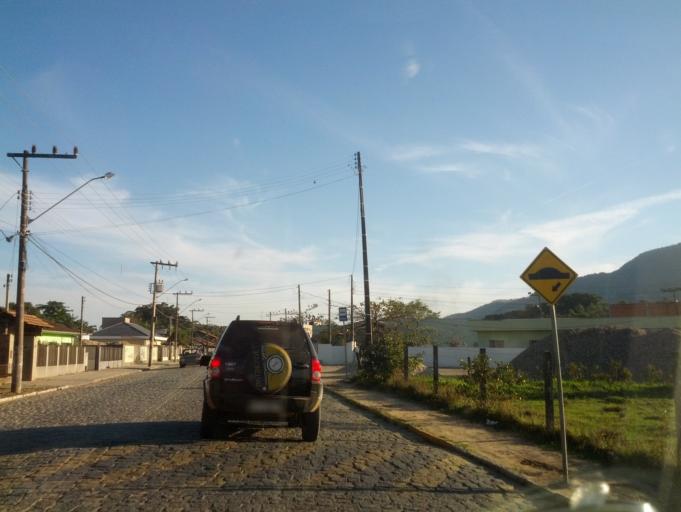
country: BR
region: Santa Catarina
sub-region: Indaial
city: Indaial
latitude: -26.9028
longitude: -49.2587
